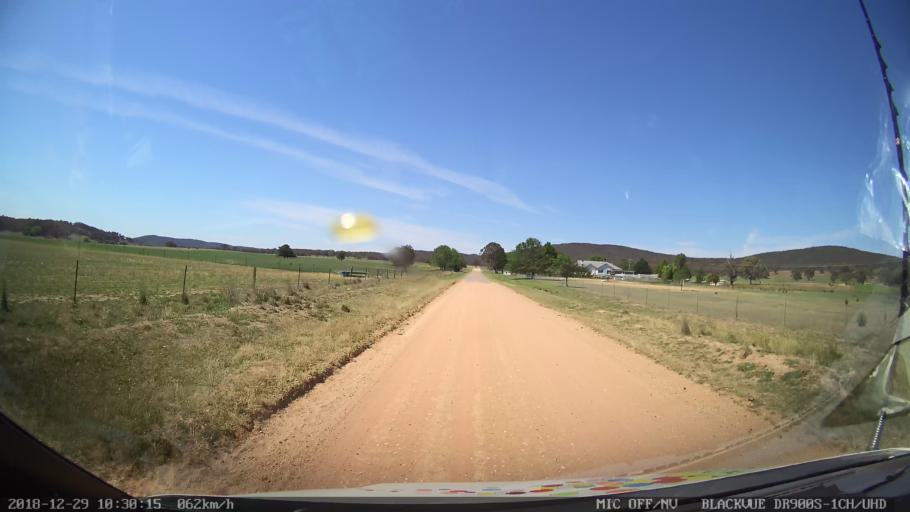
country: AU
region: New South Wales
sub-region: Yass Valley
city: Gundaroo
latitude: -34.9587
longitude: 149.4550
